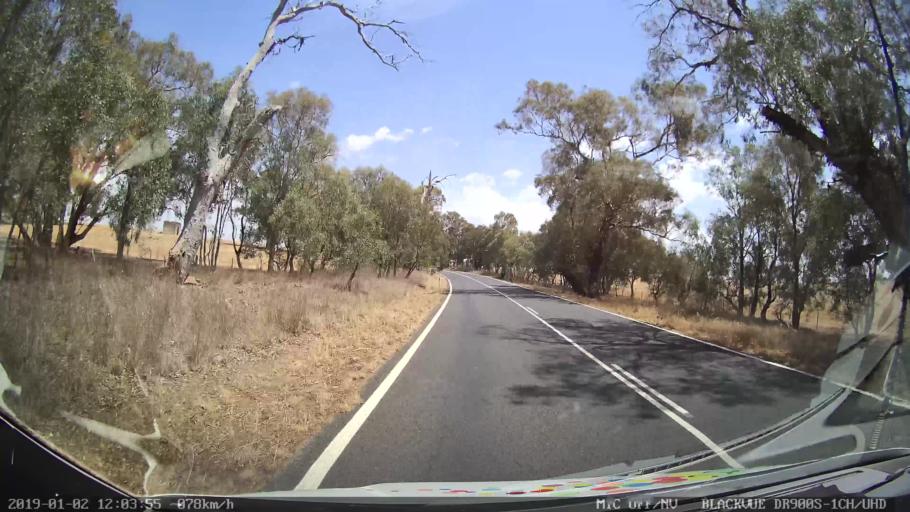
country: AU
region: New South Wales
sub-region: Young
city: Young
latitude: -34.5280
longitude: 148.3170
